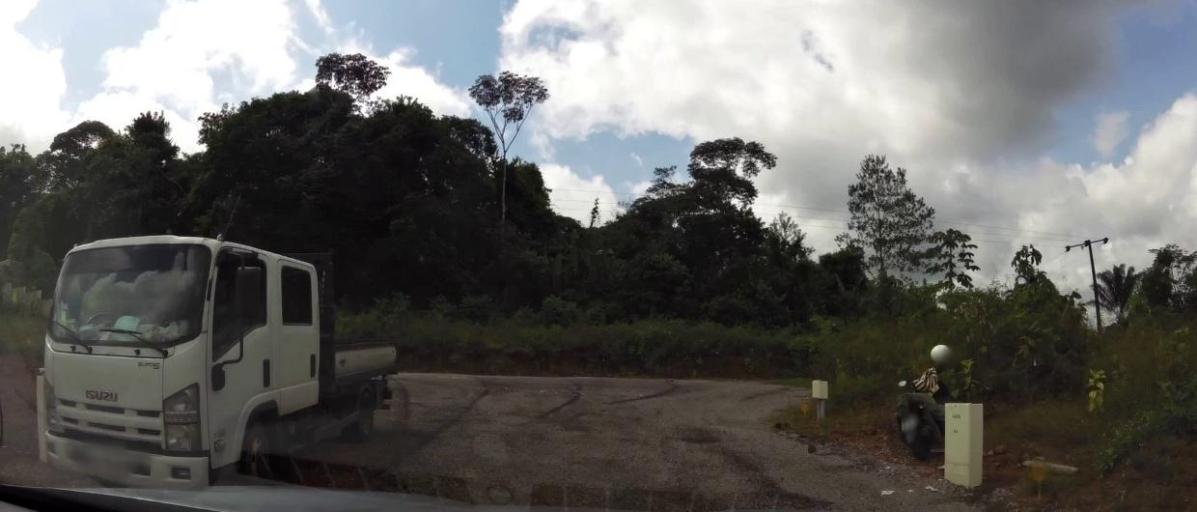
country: GF
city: Macouria
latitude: 4.8776
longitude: -52.3594
